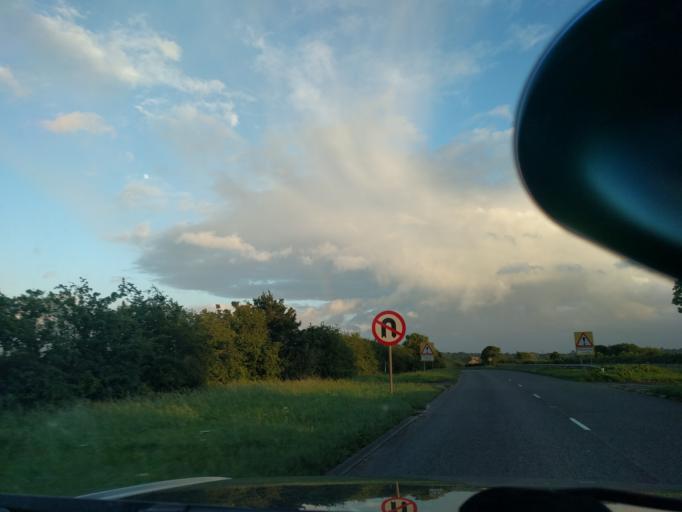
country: GB
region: England
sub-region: Wiltshire
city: Chippenham
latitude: 51.5033
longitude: -2.1259
